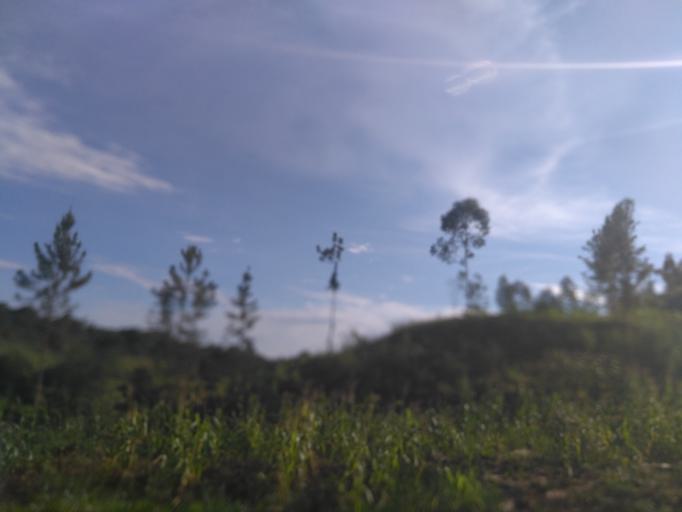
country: UG
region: Eastern Region
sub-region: Jinja District
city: Jinja
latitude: 0.4631
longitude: 33.1819
